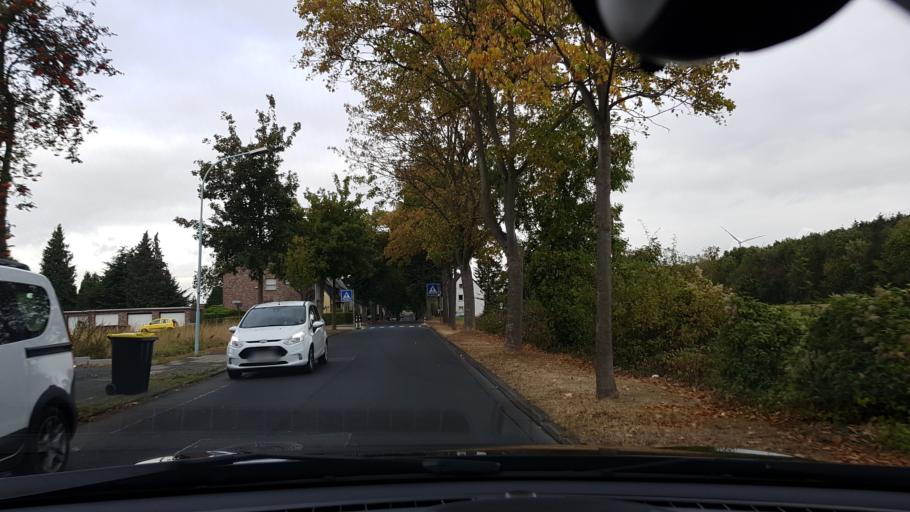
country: DE
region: North Rhine-Westphalia
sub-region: Regierungsbezirk Koln
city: Bergheim
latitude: 50.9583
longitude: 6.6453
